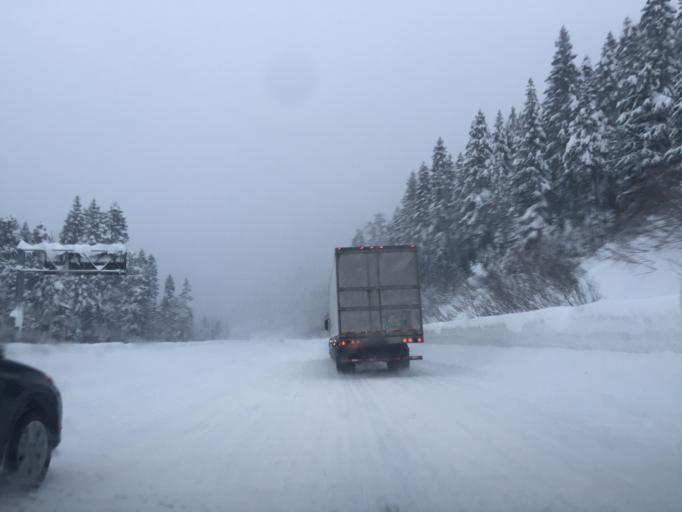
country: US
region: Washington
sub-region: Chelan County
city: Leavenworth
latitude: 47.7481
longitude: -121.0848
